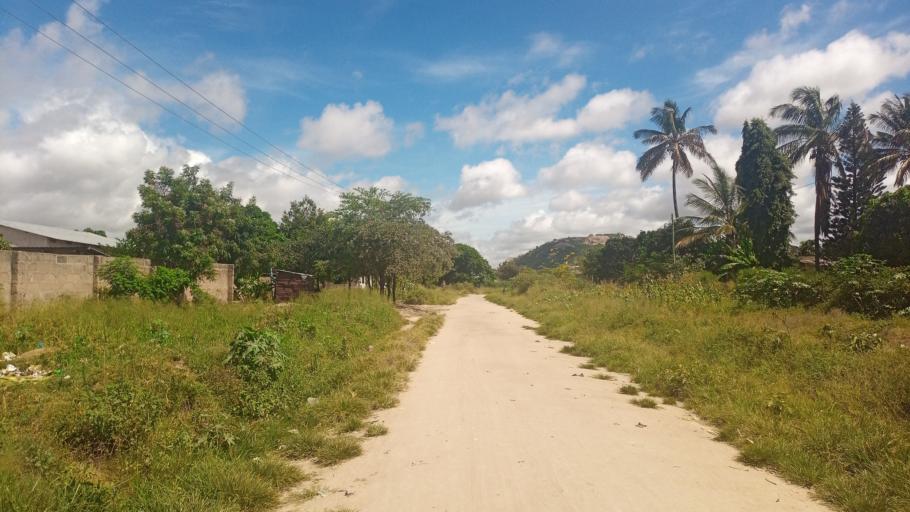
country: TZ
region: Dodoma
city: Dodoma
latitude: -6.1944
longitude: 35.7252
